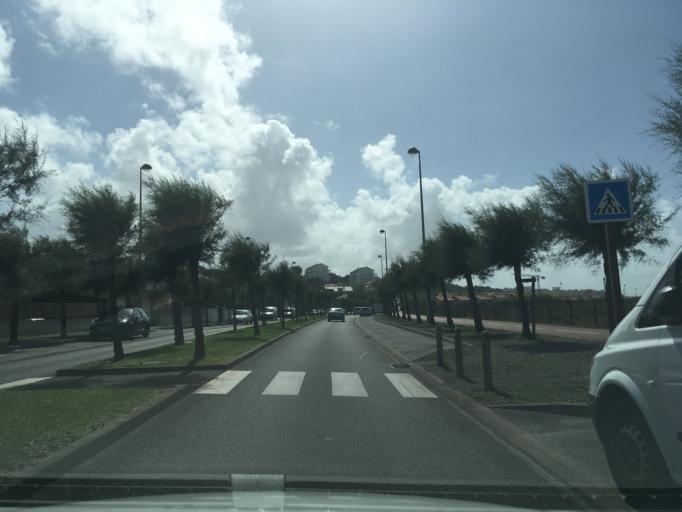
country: FR
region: Aquitaine
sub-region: Departement des Pyrenees-Atlantiques
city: Biarritz
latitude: 43.5027
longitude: -1.5368
